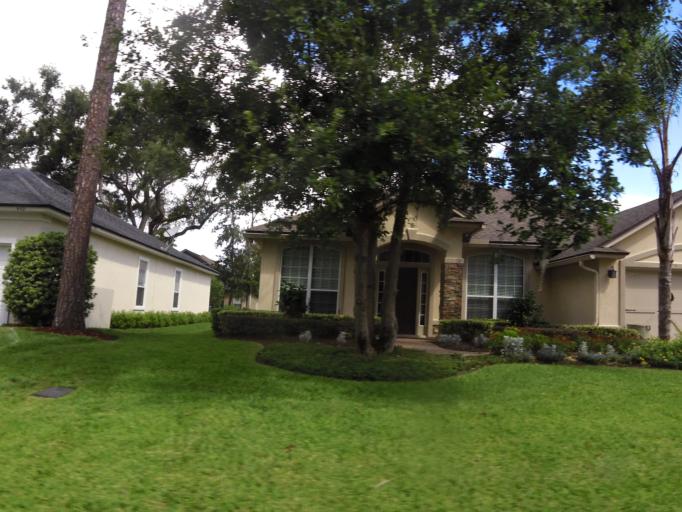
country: US
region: Florida
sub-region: Nassau County
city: Fernandina Beach
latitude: 30.6257
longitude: -81.4609
